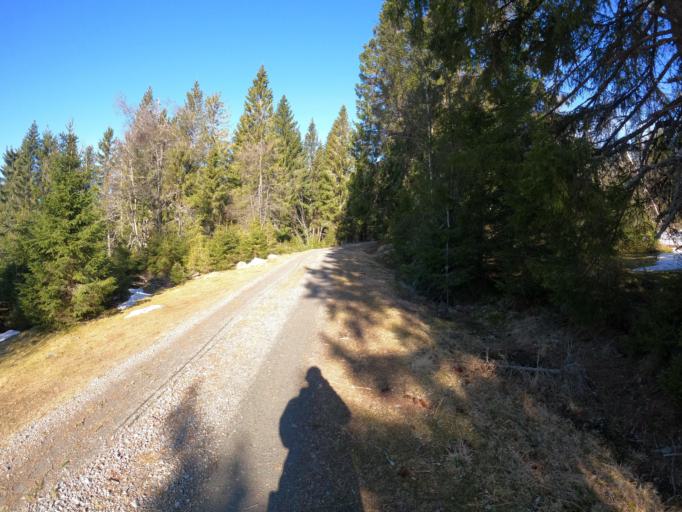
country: NO
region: Akershus
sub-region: Nittedal
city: Aneby
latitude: 60.1771
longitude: 10.9027
